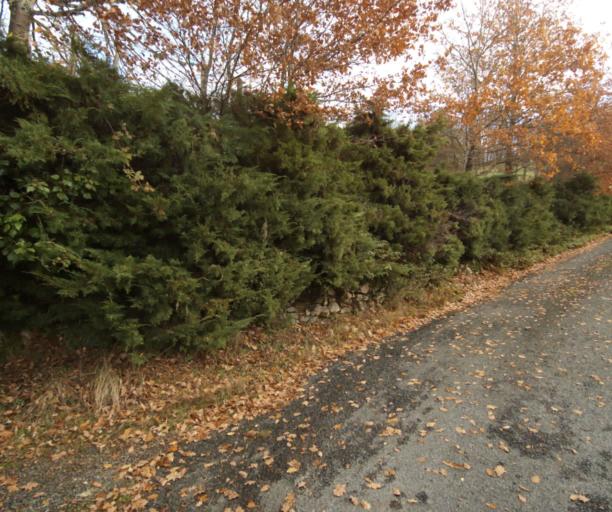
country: FR
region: Limousin
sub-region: Departement de la Correze
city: Laguenne
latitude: 45.2370
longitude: 1.7856
